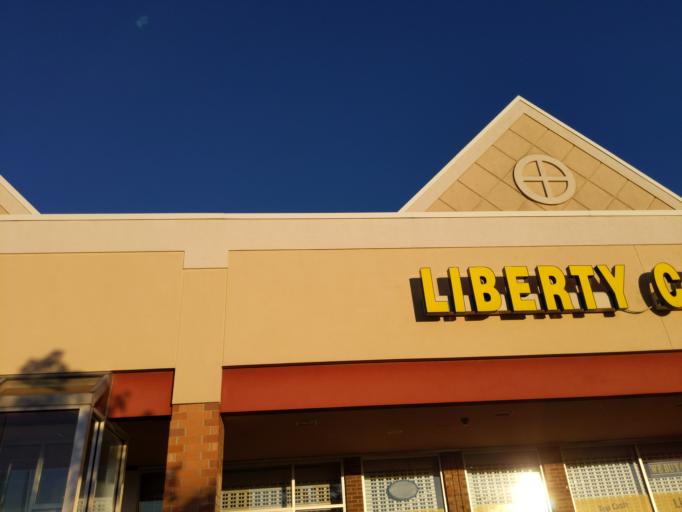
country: US
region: Michigan
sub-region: Ingham County
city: East Lansing
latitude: 42.7376
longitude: -84.5056
